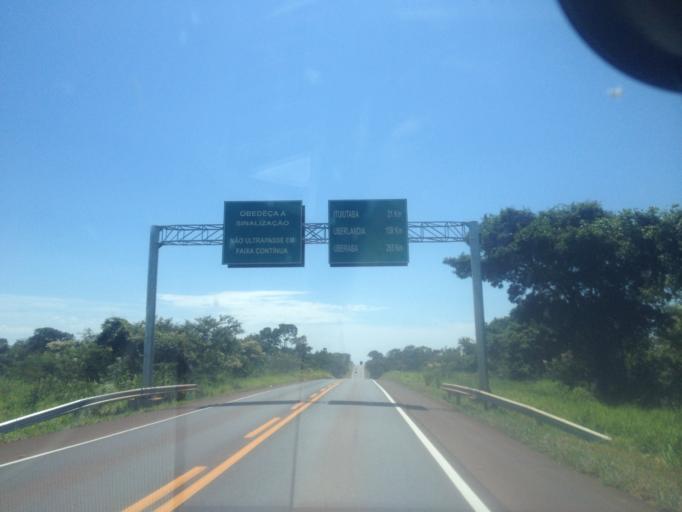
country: BR
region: Minas Gerais
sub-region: Ituiutaba
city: Ituiutaba
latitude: -18.9583
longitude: -49.6859
